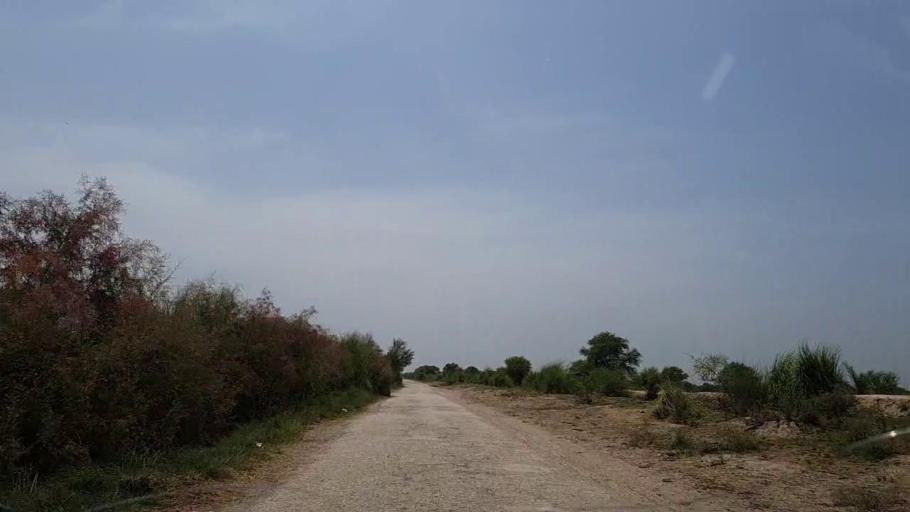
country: PK
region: Sindh
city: Khanpur
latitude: 27.8495
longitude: 69.4856
